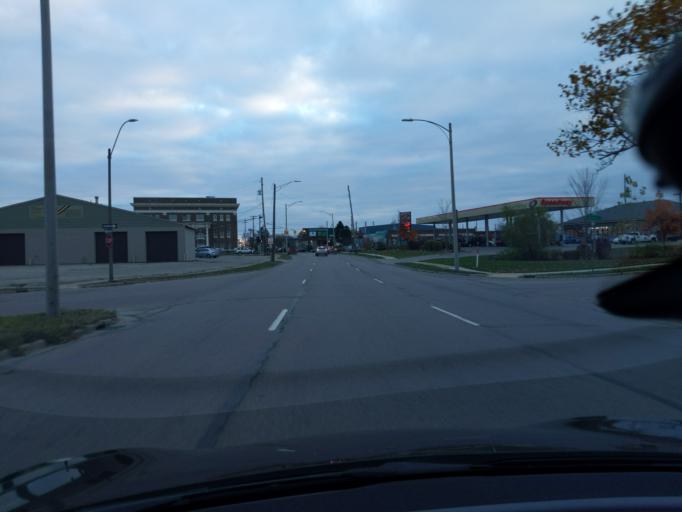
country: US
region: Michigan
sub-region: Ingham County
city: Lansing
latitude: 42.7487
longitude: -84.5462
